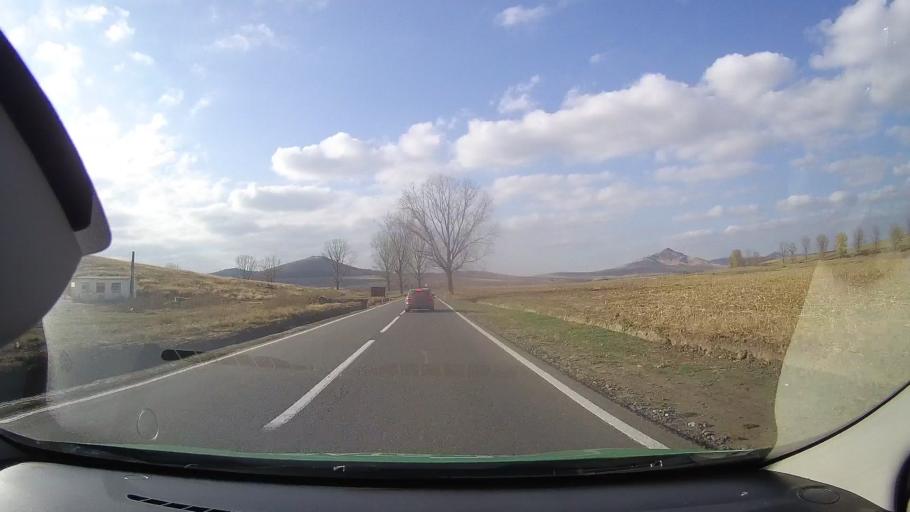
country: RO
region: Tulcea
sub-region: Comuna Nalbant
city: Nicolae Balcescu
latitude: 44.9925
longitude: 28.5682
